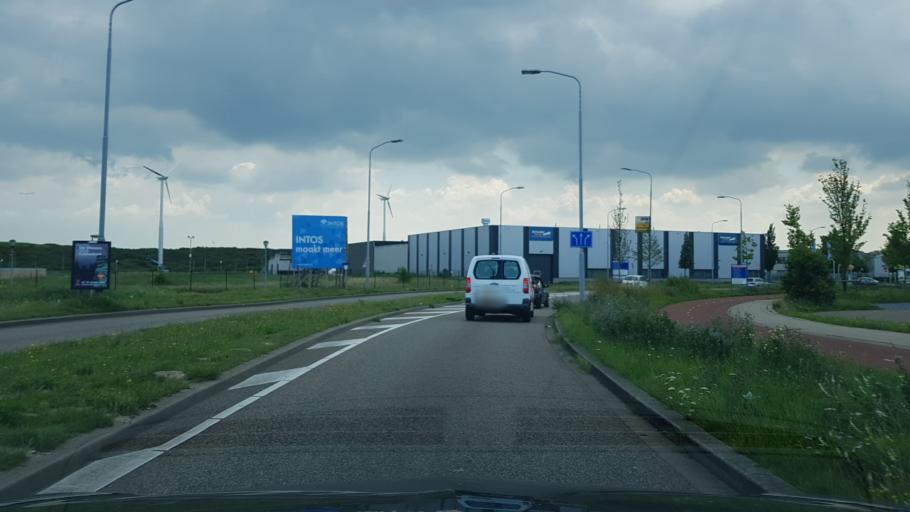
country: NL
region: North Holland
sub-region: Gemeente Haarlem
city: Haarlem
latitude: 52.4005
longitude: 4.6600
